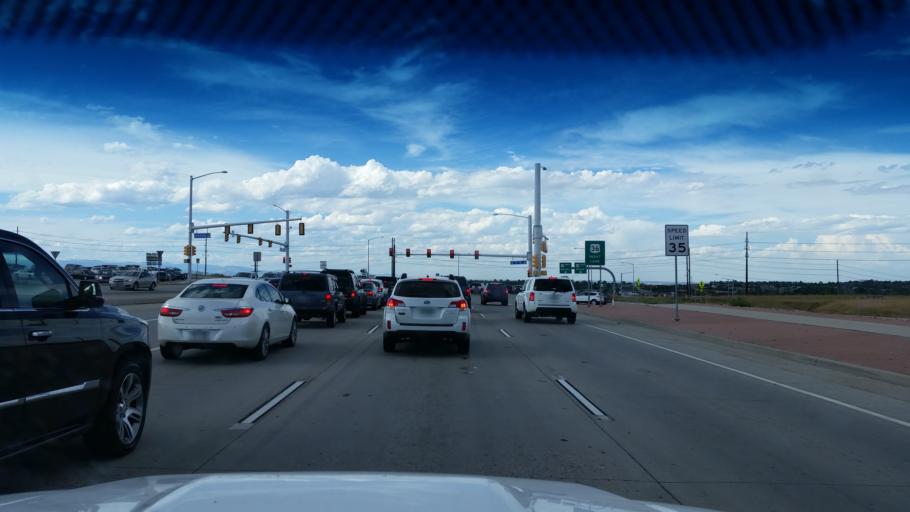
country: US
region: Colorado
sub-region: Broomfield County
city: Broomfield
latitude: 39.9125
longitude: -105.0968
